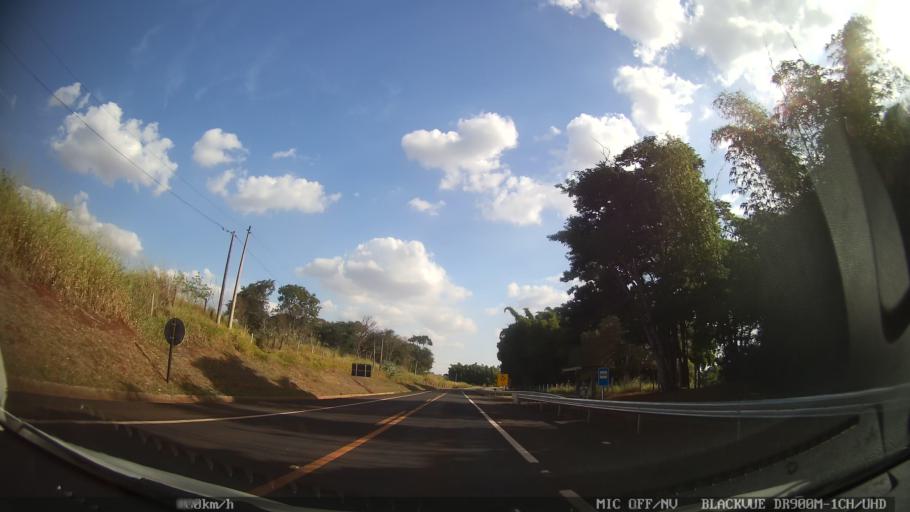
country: BR
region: Sao Paulo
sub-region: Ribeirao Preto
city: Ribeirao Preto
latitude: -21.1948
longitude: -47.8719
